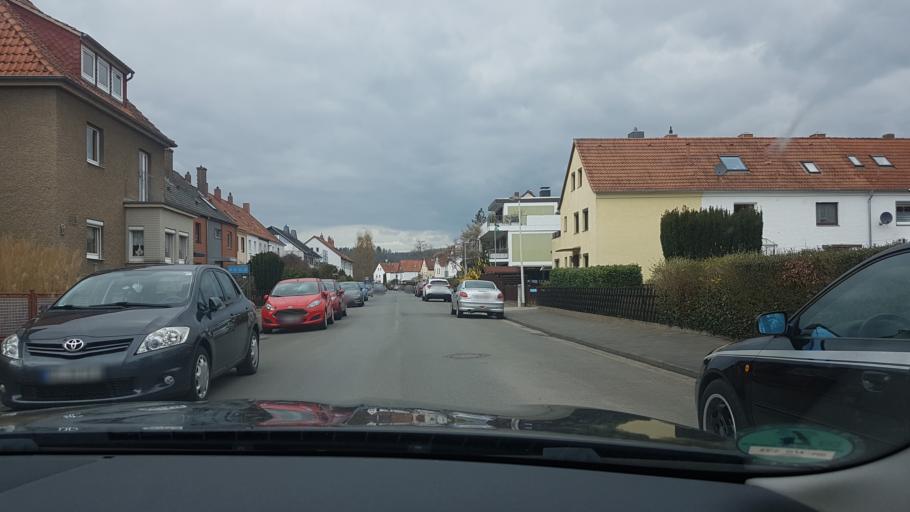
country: DE
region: Lower Saxony
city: Hameln
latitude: 52.1175
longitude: 9.3534
